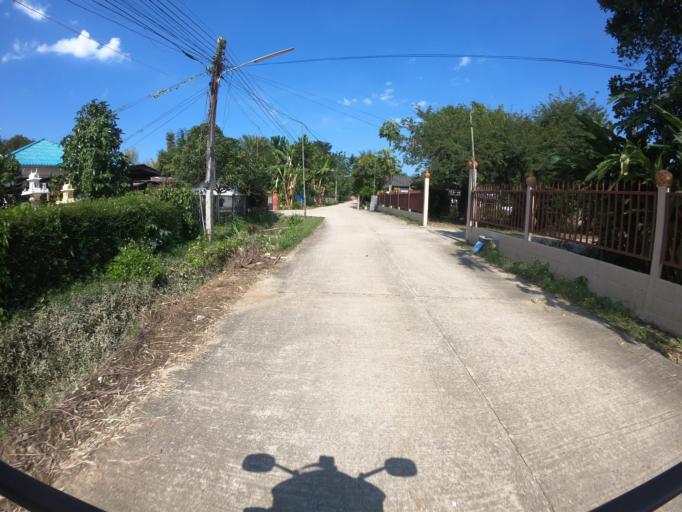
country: TH
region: Chiang Mai
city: San Sai
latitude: 18.8729
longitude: 98.9758
